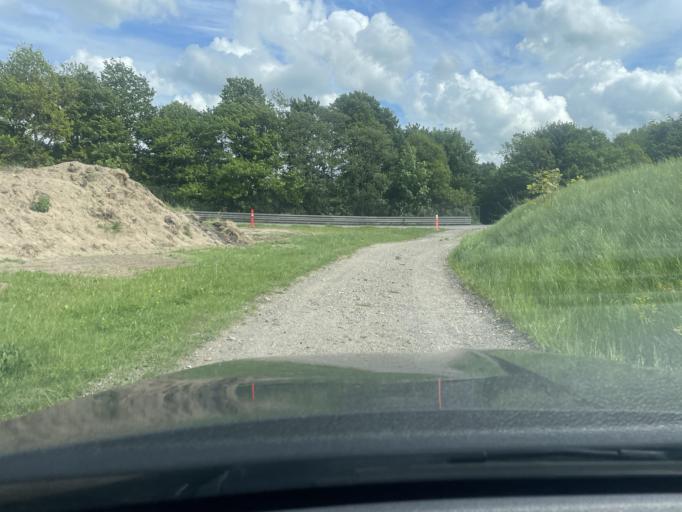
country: DK
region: Central Jutland
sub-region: Viborg Kommune
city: Viborg
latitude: 56.5354
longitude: 9.4560
